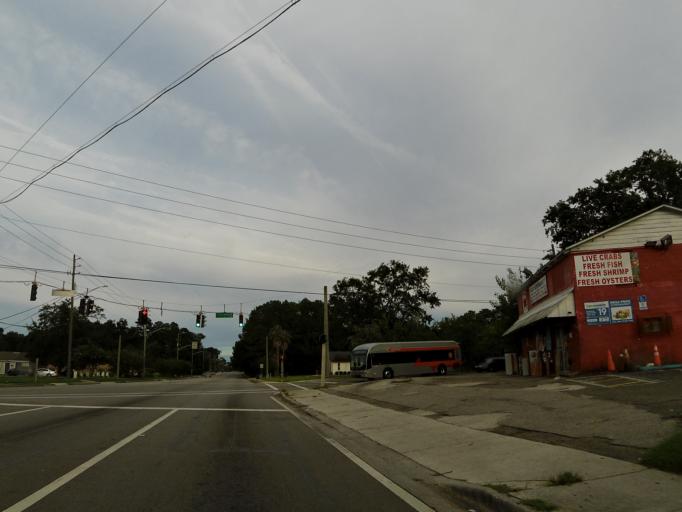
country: US
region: Florida
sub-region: Duval County
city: Jacksonville
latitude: 30.3876
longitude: -81.7159
